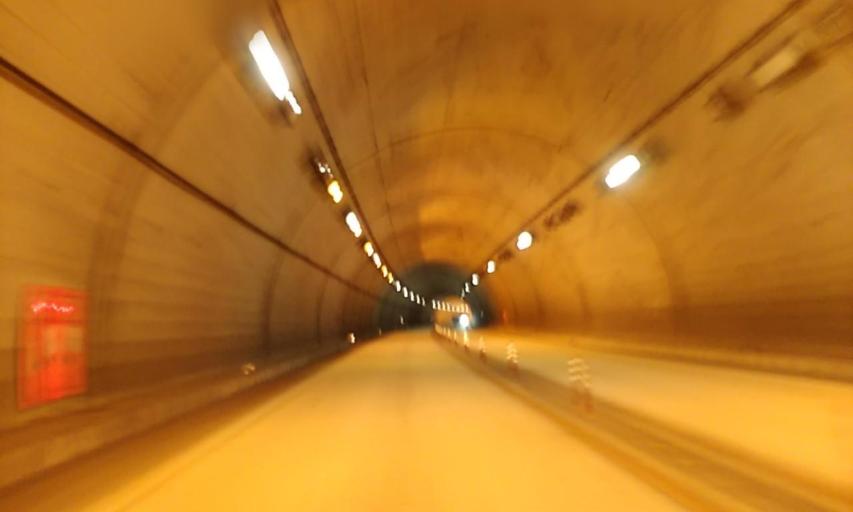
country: JP
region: Wakayama
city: Shingu
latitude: 33.6883
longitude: 135.9581
